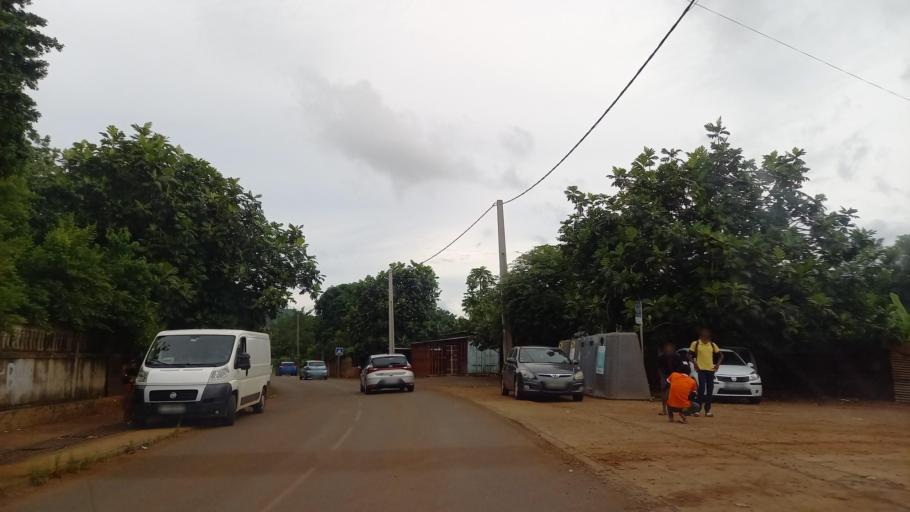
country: YT
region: Chirongui
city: Chirongui
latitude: -12.9057
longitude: 45.1511
